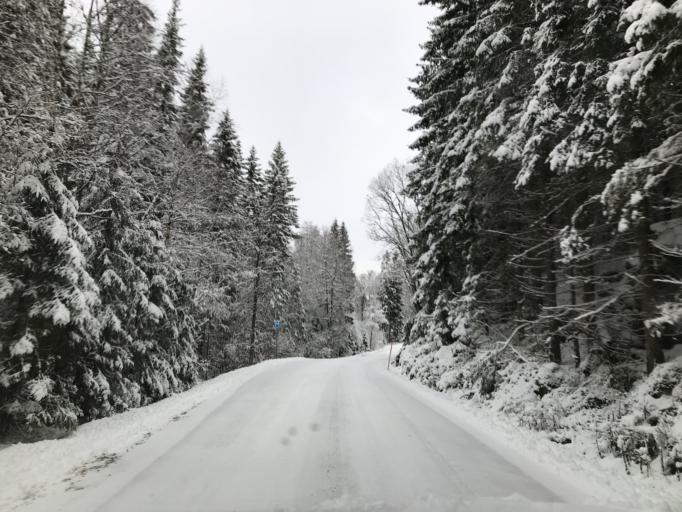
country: SE
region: Vaestra Goetaland
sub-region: Boras Kommun
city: Sandared
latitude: 57.8065
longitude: 12.7237
